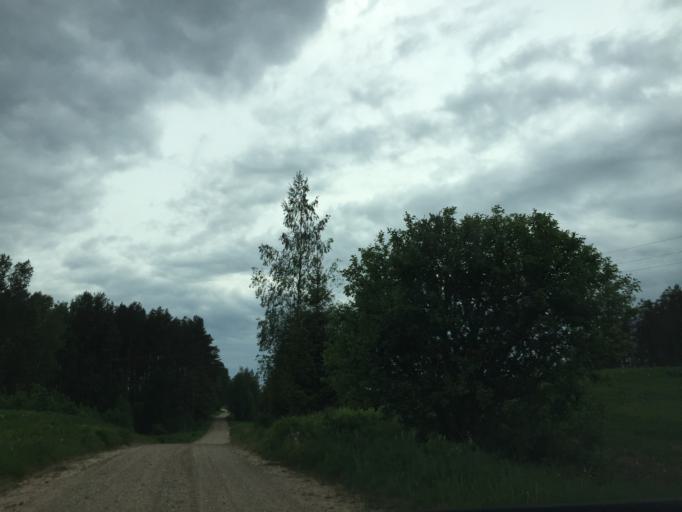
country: LV
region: Aglona
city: Aglona
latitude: 56.1584
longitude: 27.2335
